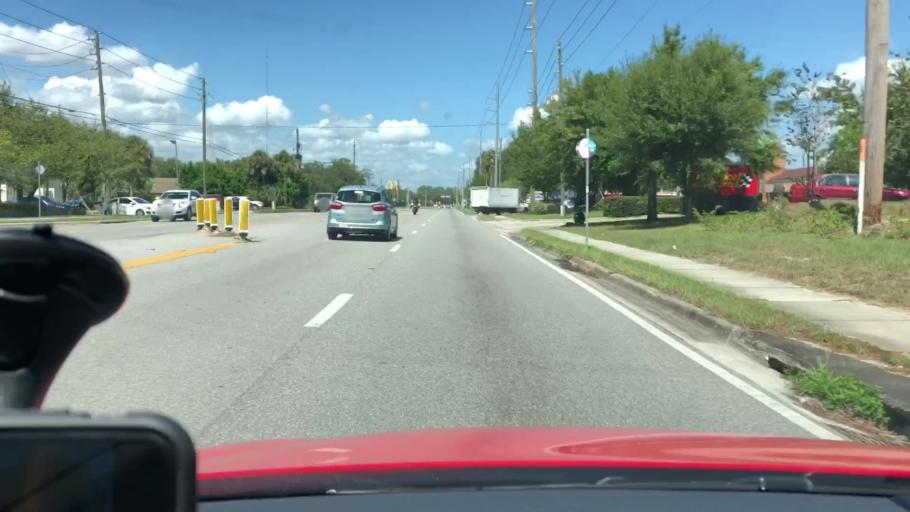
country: US
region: Florida
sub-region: Volusia County
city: Orange City
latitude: 28.9188
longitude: -81.2960
